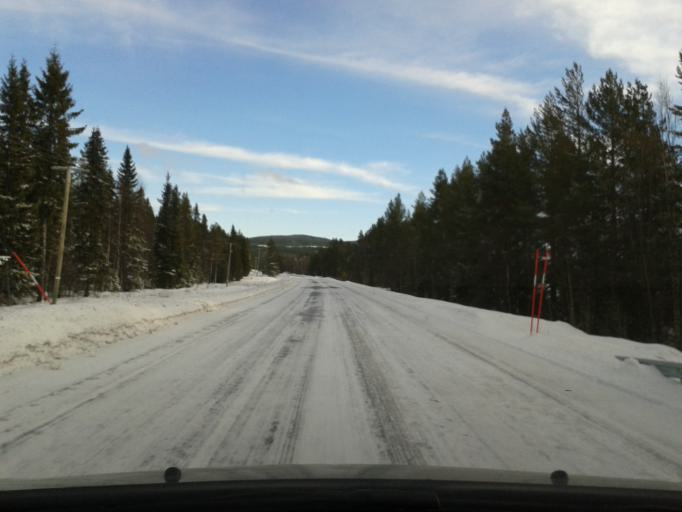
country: SE
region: Vaesterbotten
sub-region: Asele Kommun
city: Asele
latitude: 64.3412
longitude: 17.0208
